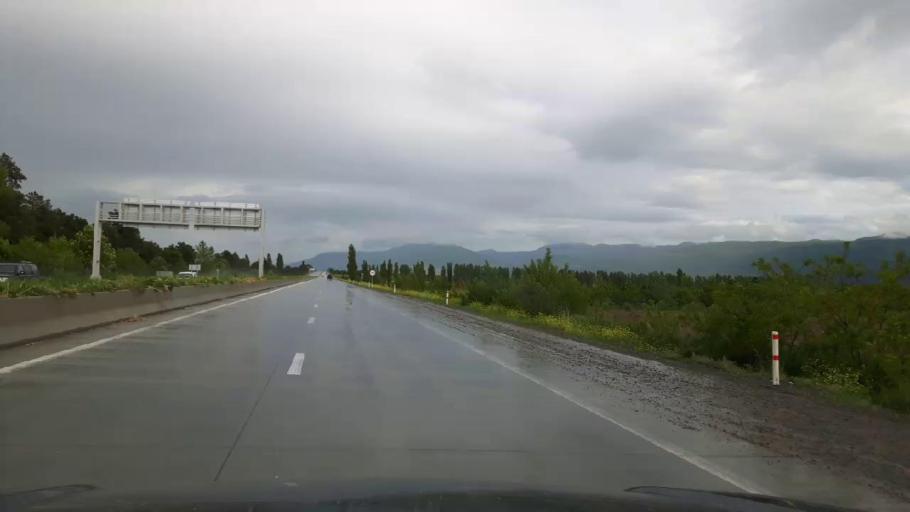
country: GE
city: Agara
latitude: 42.0462
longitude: 43.9185
